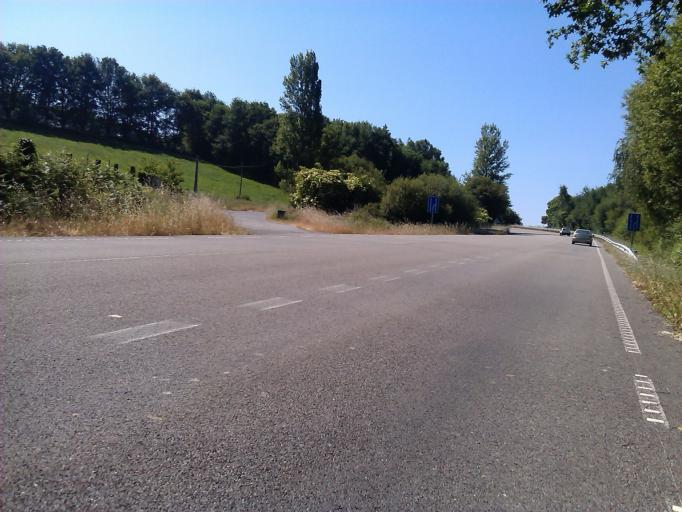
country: ES
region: Galicia
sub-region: Provincia de Lugo
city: Samos
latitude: 42.7335
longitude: -7.3547
